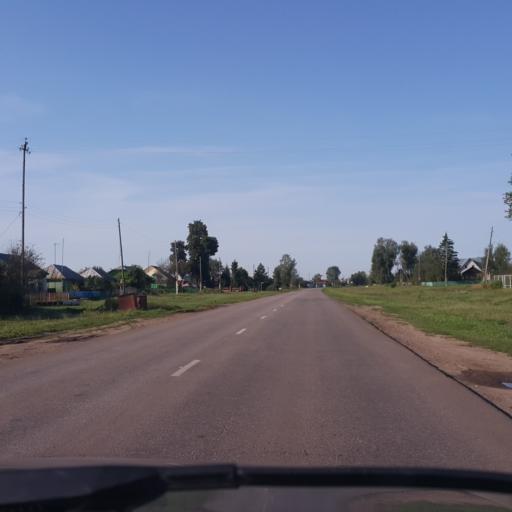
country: RU
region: Tambov
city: Novaya Lyada
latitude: 52.7795
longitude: 41.7596
